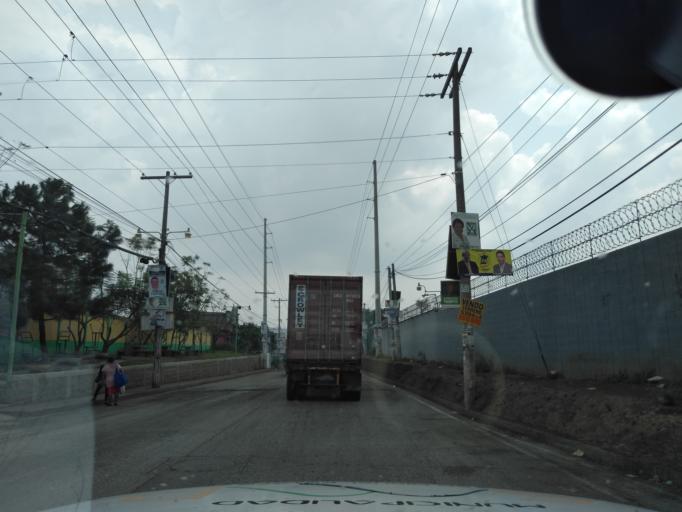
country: GT
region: Guatemala
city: Petapa
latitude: 14.5067
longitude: -90.5596
